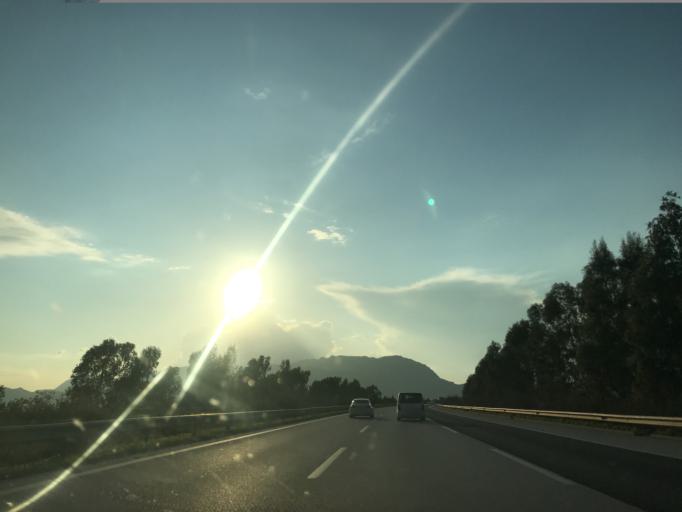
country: TR
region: Adana
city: Ceyhan
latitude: 36.9823
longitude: 35.7887
